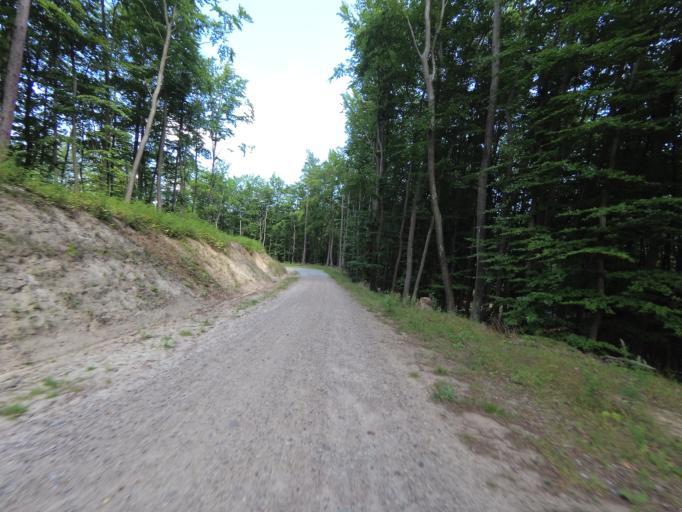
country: PL
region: Pomeranian Voivodeship
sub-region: Gdynia
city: Wielki Kack
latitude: 54.4829
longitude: 18.5026
